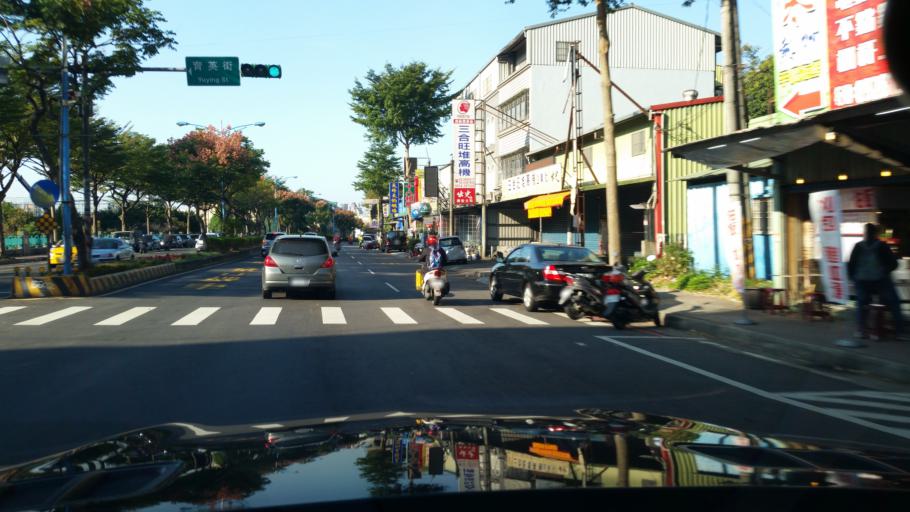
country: TW
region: Taiwan
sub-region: Taoyuan
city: Taoyuan
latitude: 24.9991
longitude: 121.3386
